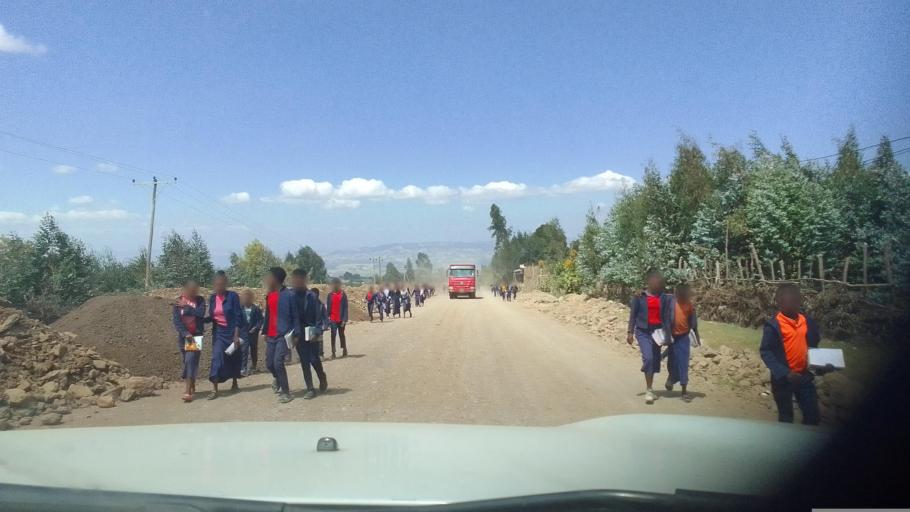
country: ET
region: Oromiya
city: Hagere Hiywet
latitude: 8.8555
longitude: 37.8926
